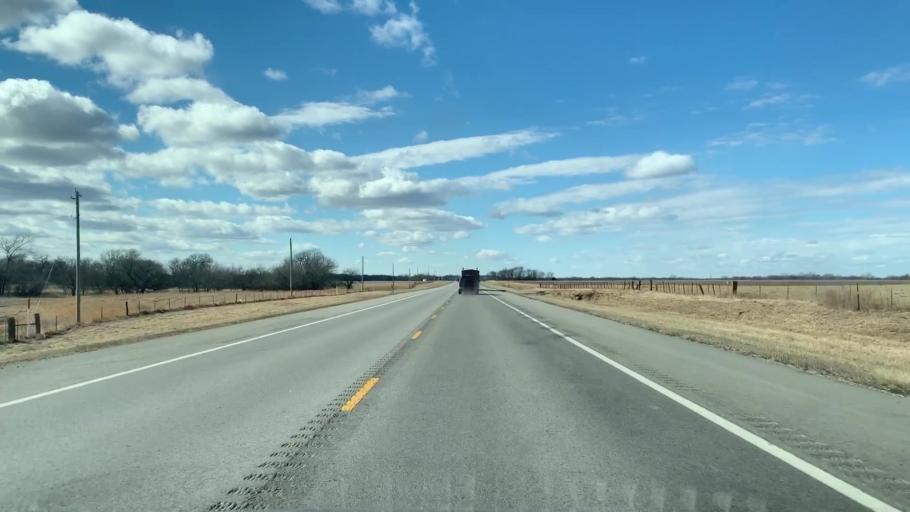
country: US
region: Kansas
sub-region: Crawford County
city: Pittsburg
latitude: 37.3397
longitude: -94.8596
